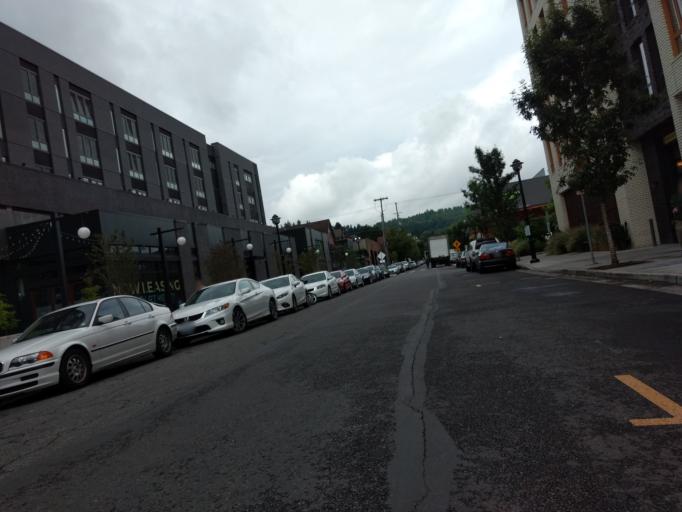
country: US
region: Oregon
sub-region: Multnomah County
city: Portland
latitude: 45.5334
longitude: -122.6949
